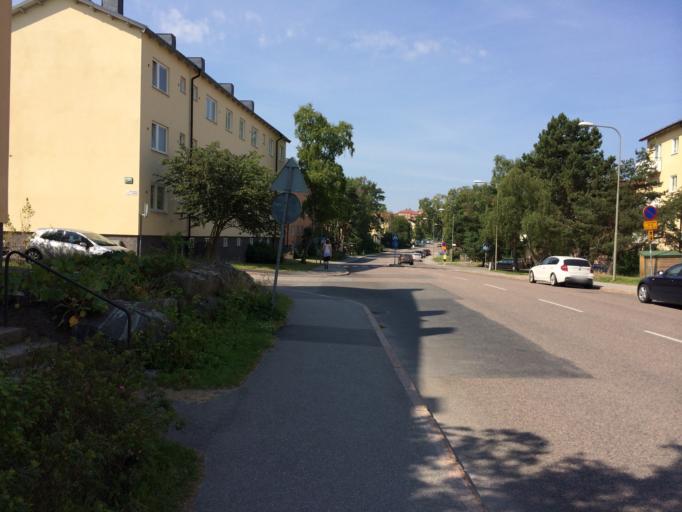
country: SE
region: Stockholm
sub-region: Stockholms Kommun
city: Arsta
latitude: 59.3020
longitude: 17.9930
